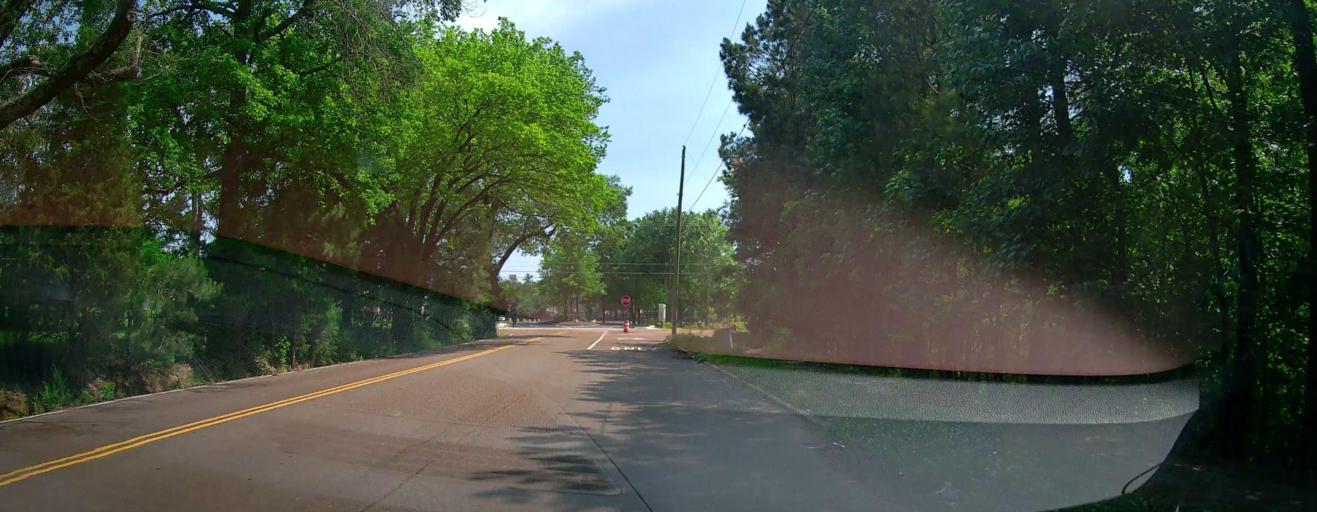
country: US
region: Mississippi
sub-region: De Soto County
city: Olive Branch
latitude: 35.0067
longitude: -89.8294
